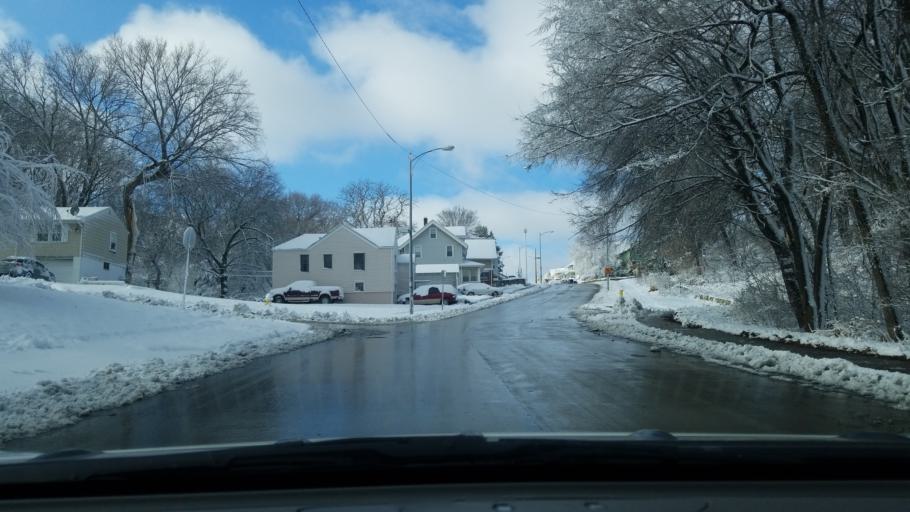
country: US
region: Nebraska
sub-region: Douglas County
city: Omaha
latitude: 41.2195
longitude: -95.9414
